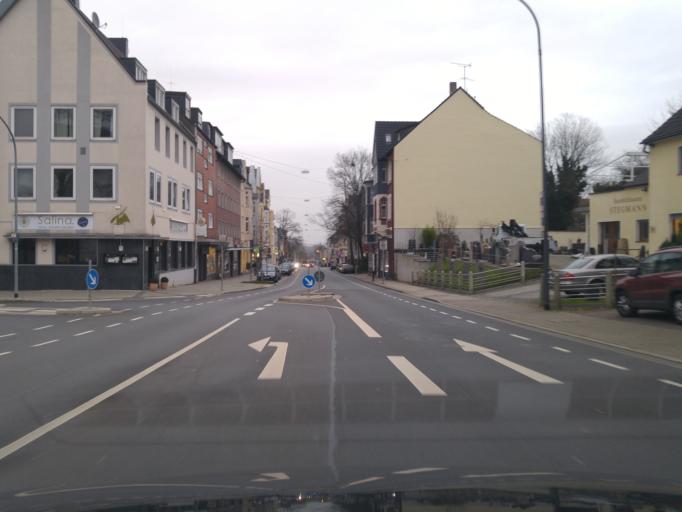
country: DE
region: North Rhine-Westphalia
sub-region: Regierungsbezirk Dusseldorf
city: Essen
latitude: 51.4252
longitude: 7.0405
